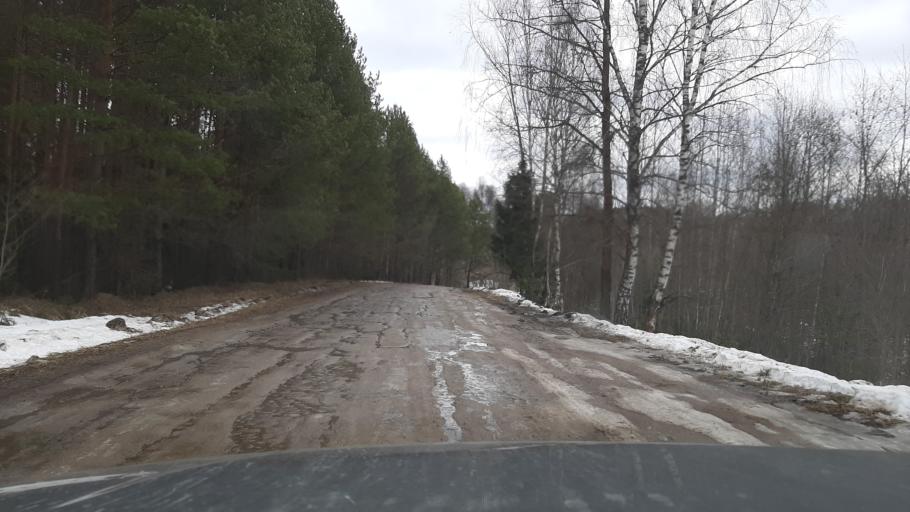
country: RU
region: Ivanovo
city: Teykovo
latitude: 56.8937
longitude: 40.6619
